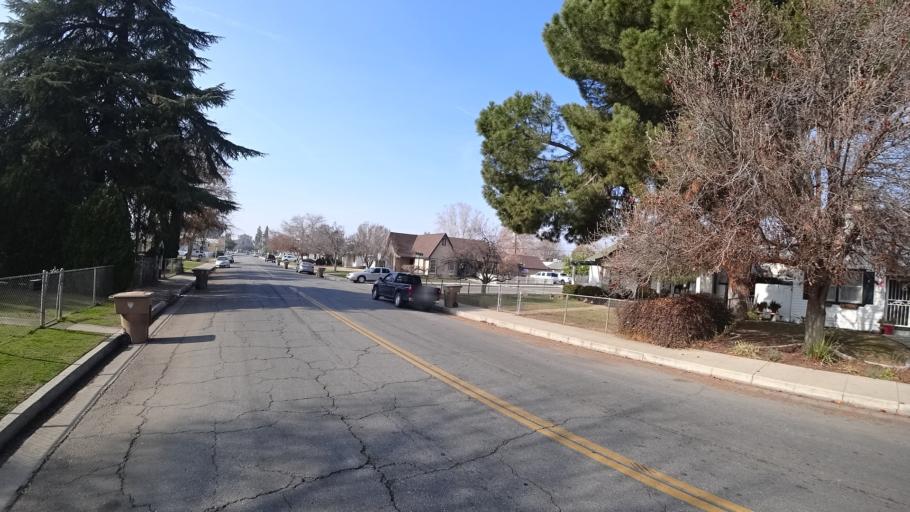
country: US
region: California
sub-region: Kern County
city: Bakersfield
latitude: 35.3650
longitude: -119.0362
